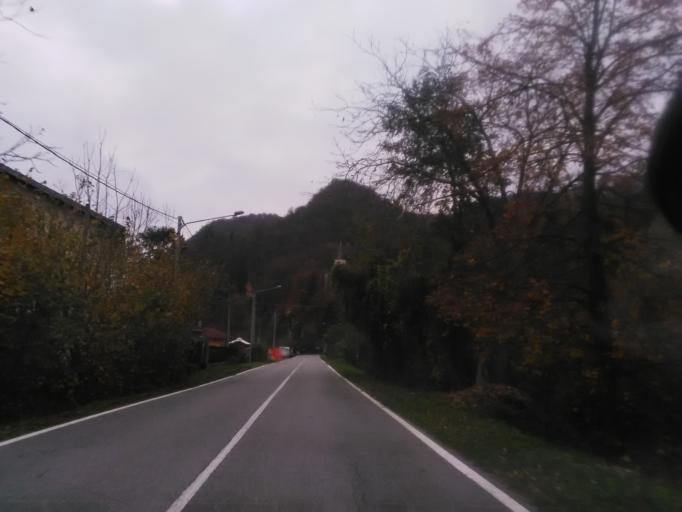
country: IT
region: Piedmont
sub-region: Provincia di Vercelli
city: Varallo
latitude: 45.8054
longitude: 8.2589
